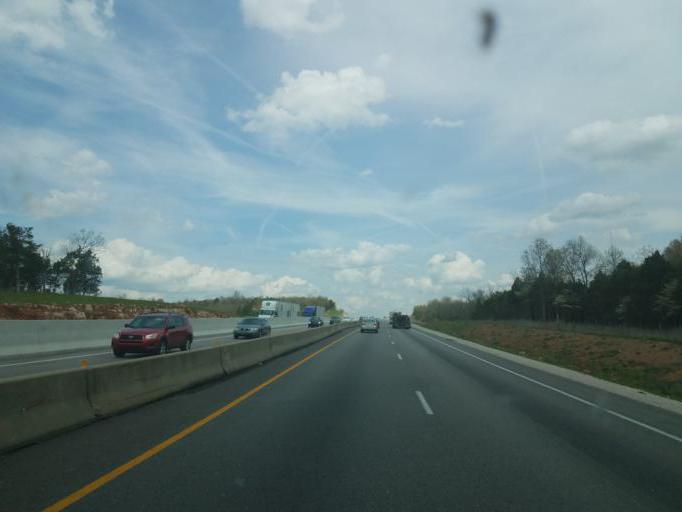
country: US
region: Kentucky
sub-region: Hart County
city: Munfordville
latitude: 37.4418
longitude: -85.8839
